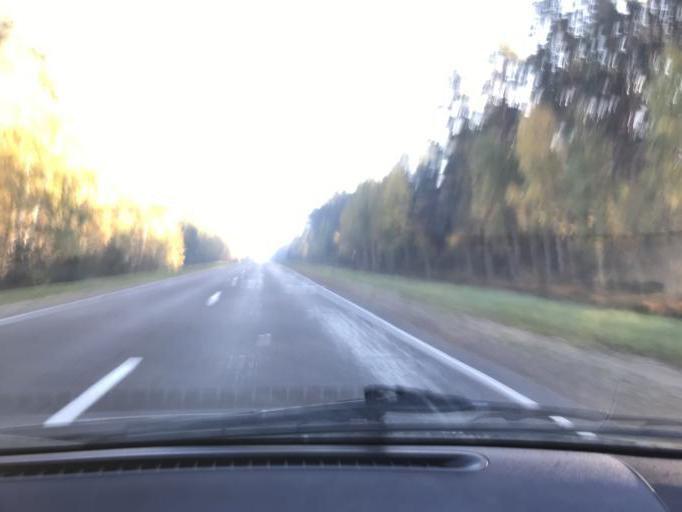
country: BY
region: Brest
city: Asnyezhytsy
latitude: 52.2433
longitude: 26.2195
